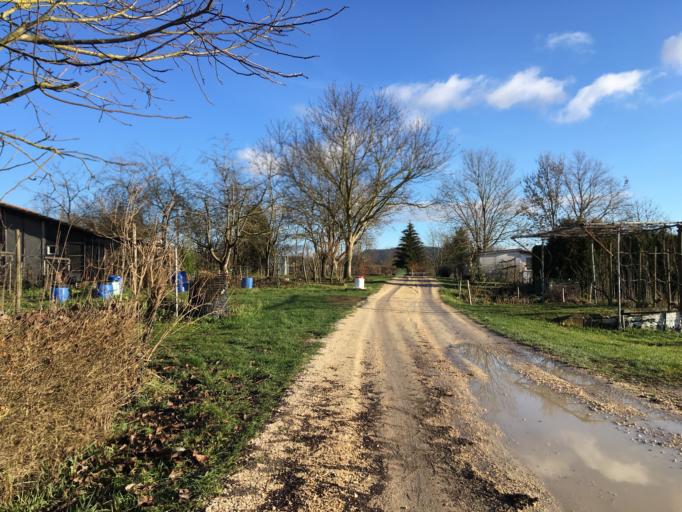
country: DE
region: Baden-Wuerttemberg
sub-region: Freiburg Region
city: Gottmadingen
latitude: 47.7231
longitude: 8.7781
